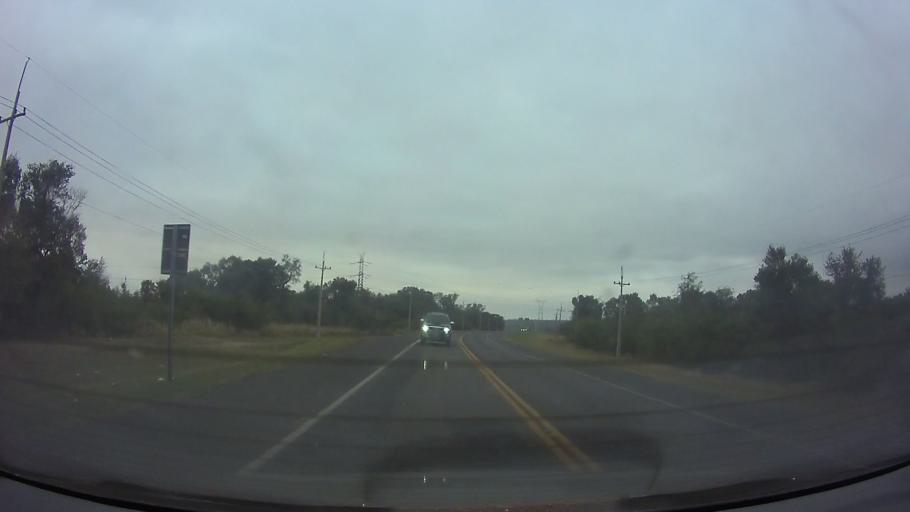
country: PY
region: Central
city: Limpio
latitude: -25.1155
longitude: -57.4258
